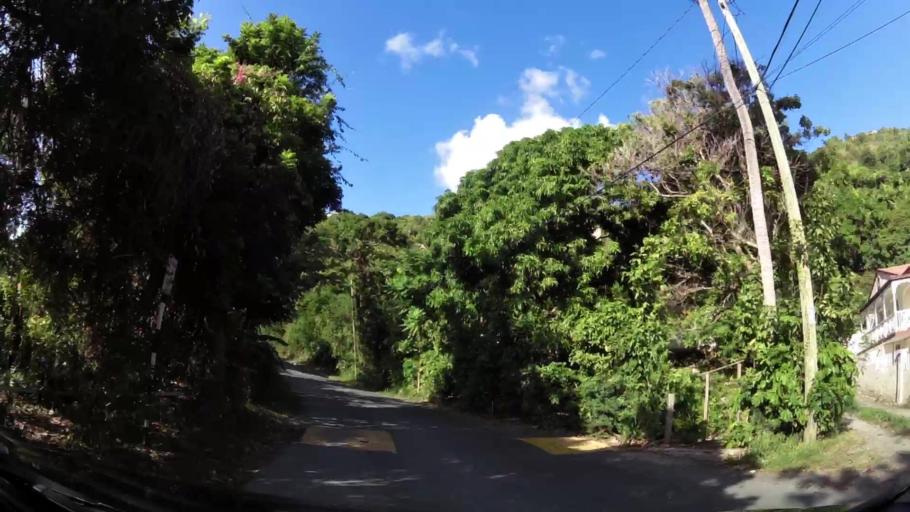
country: VG
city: Road Town
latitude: 18.4143
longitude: -64.6702
